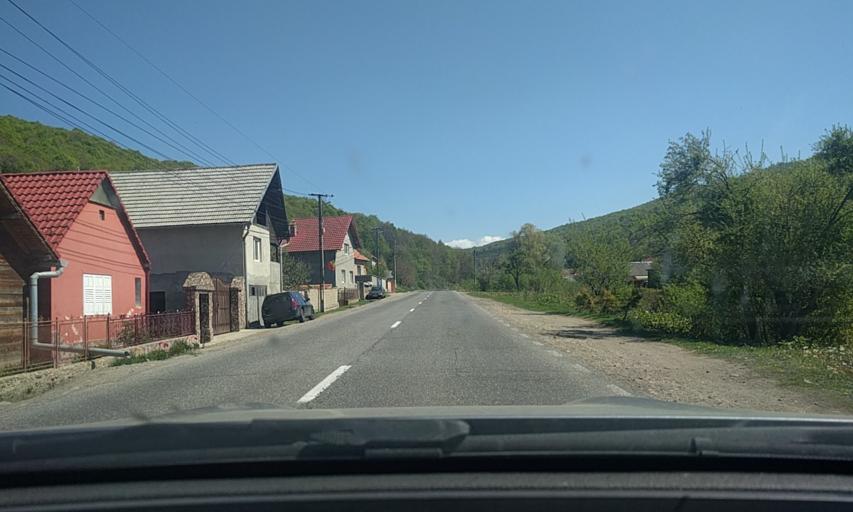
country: RO
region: Brasov
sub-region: Comuna Teliu
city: Teliu
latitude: 45.6868
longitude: 25.8969
